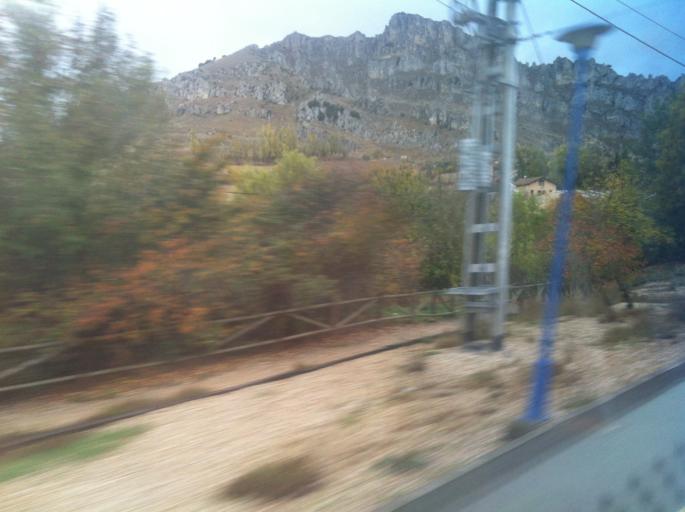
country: ES
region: Castille and Leon
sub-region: Provincia de Burgos
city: Pancorbo
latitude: 42.6307
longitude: -3.1126
